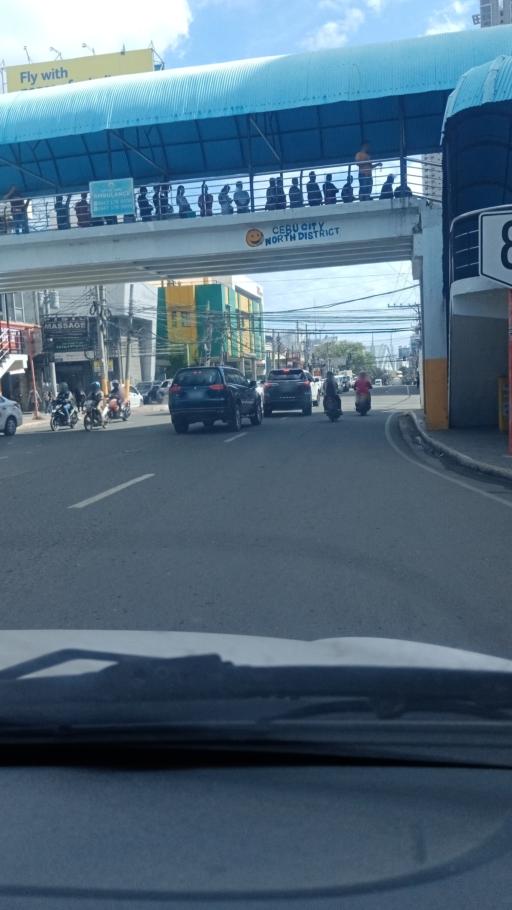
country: PH
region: Central Visayas
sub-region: Province of Cebu
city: Cebu City
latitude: 10.3097
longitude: 123.8940
